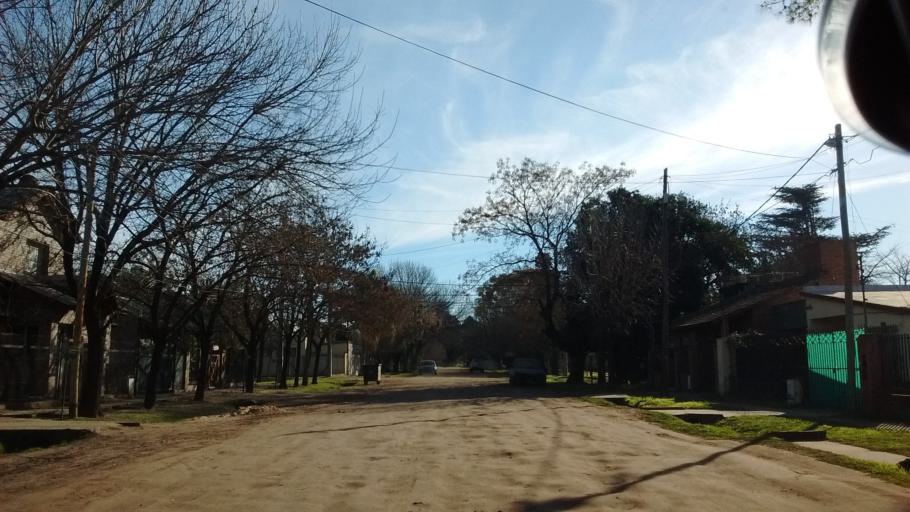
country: AR
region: Santa Fe
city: Funes
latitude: -32.9124
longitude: -60.8171
